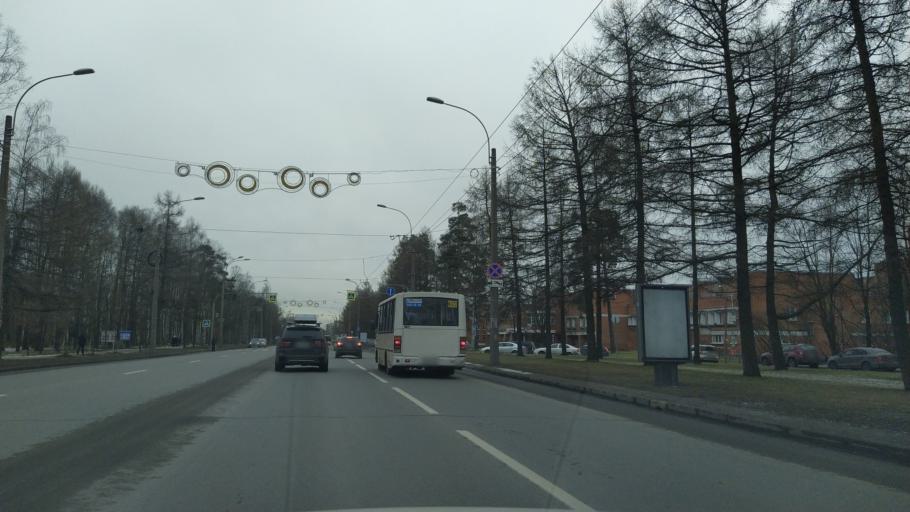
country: RU
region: St.-Petersburg
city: Sosnovka
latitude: 60.0154
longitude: 30.3396
